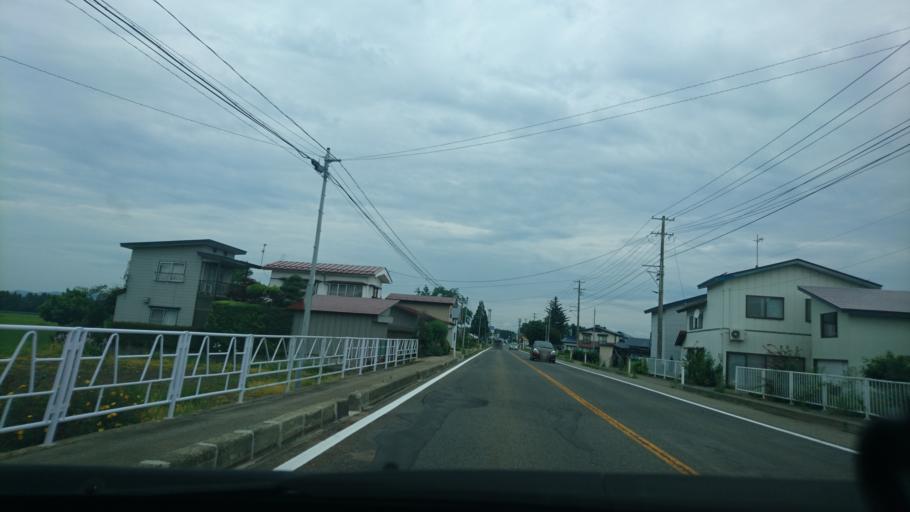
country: JP
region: Akita
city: Omagari
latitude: 39.4069
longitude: 140.5577
